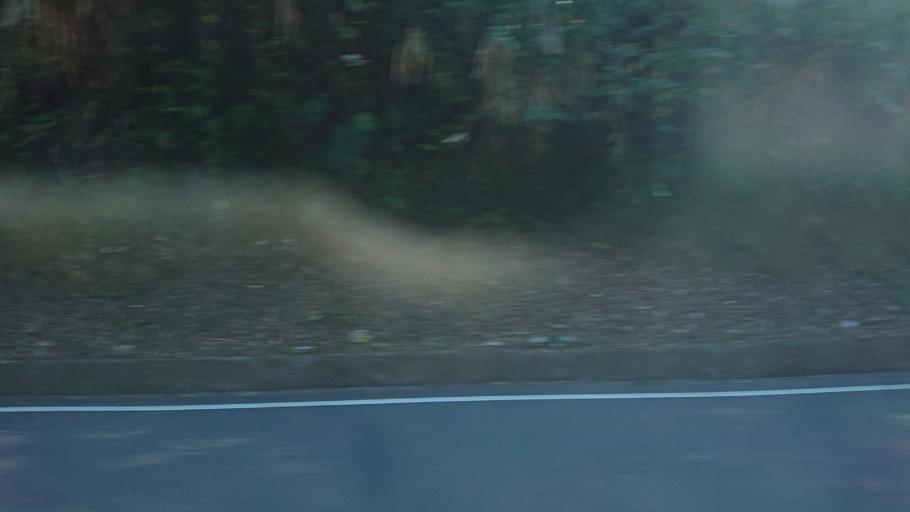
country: TW
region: Taiwan
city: Lugu
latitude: 23.4873
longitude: 120.7488
